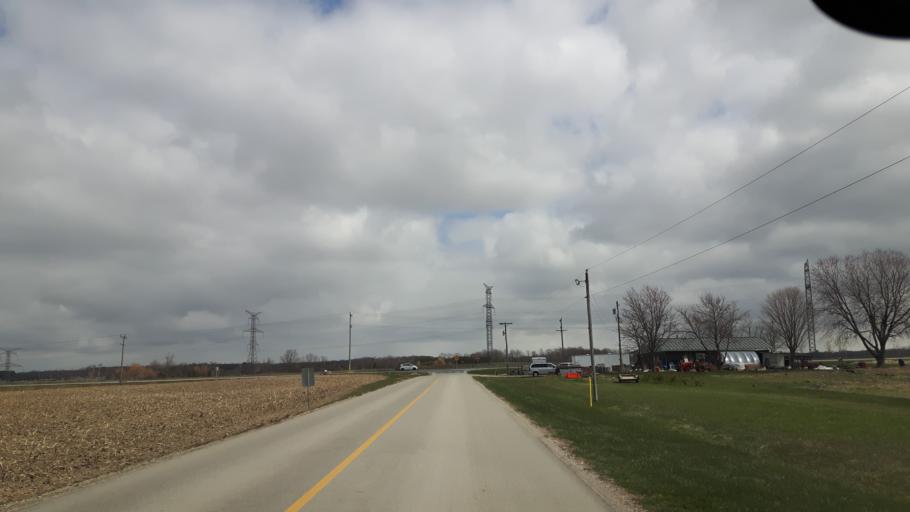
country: CA
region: Ontario
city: Goderich
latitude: 43.7102
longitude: -81.6632
